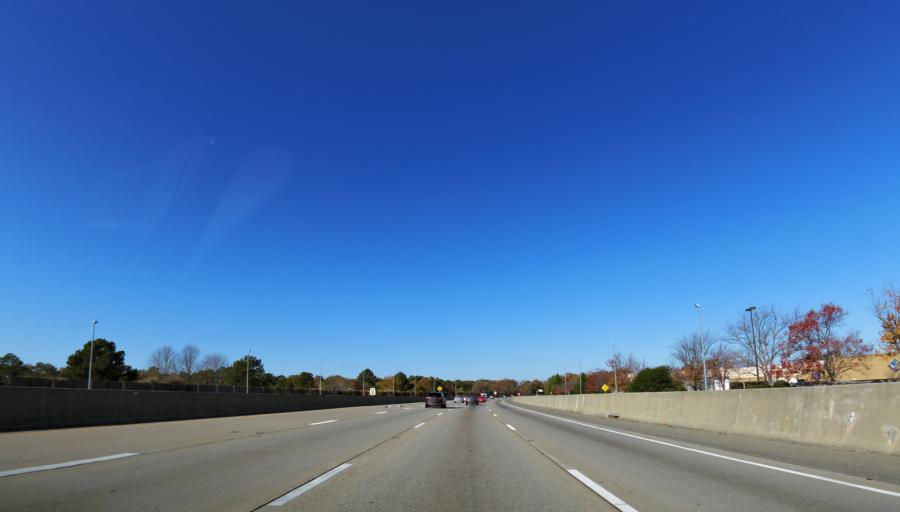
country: US
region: Virginia
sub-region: York County
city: Yorktown
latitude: 37.1178
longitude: -76.5079
